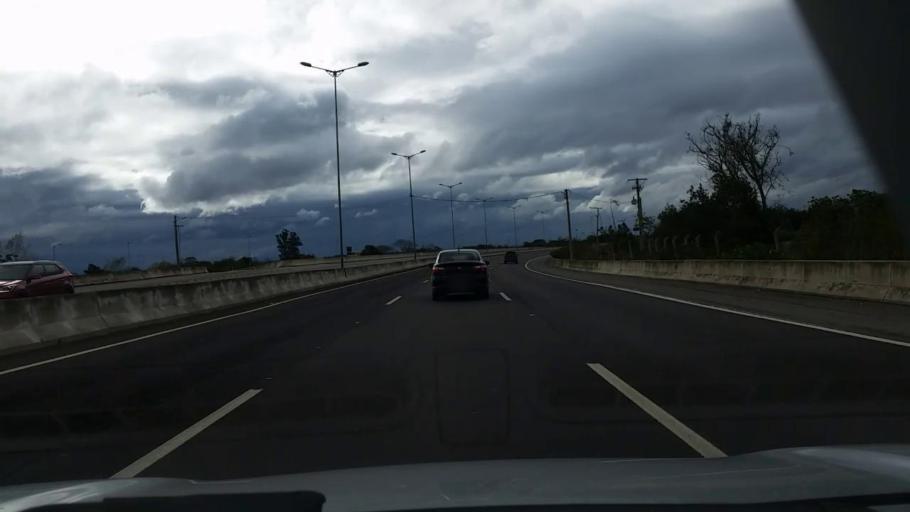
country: BR
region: Rio Grande do Sul
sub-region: Canoas
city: Canoas
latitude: -29.9647
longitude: -51.2024
